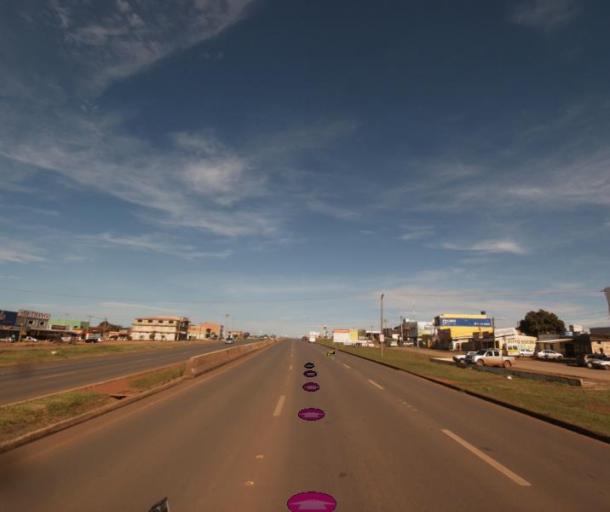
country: BR
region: Federal District
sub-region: Brasilia
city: Brasilia
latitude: -15.7354
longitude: -48.2807
